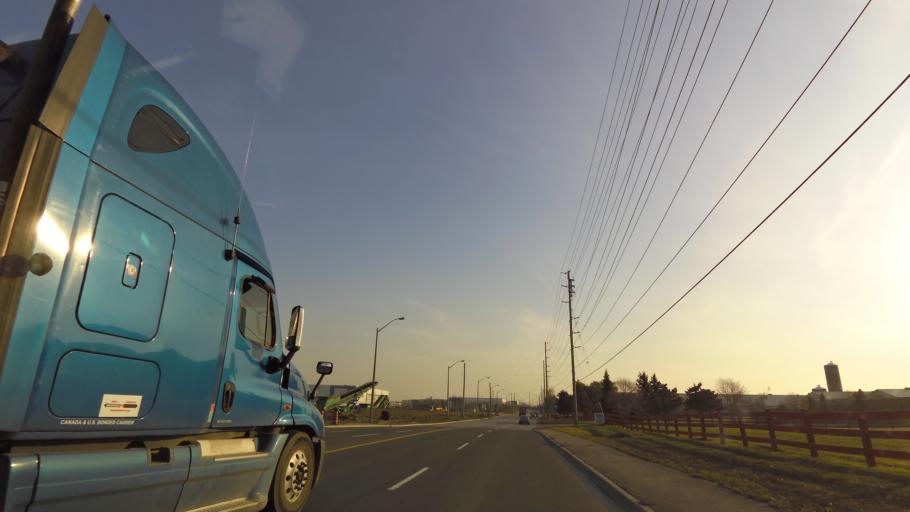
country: CA
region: Ontario
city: Brampton
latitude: 43.7858
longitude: -79.6510
